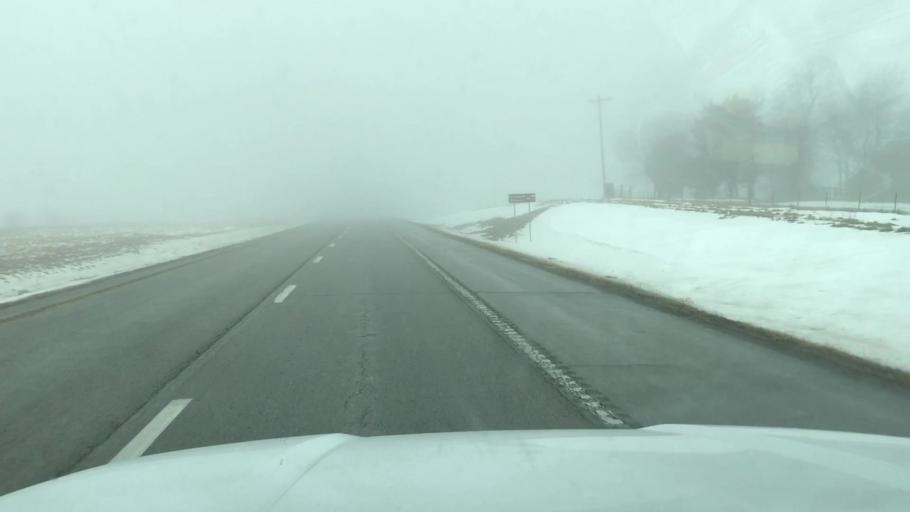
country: US
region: Missouri
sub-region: Clinton County
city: Cameron
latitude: 39.7549
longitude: -94.2981
